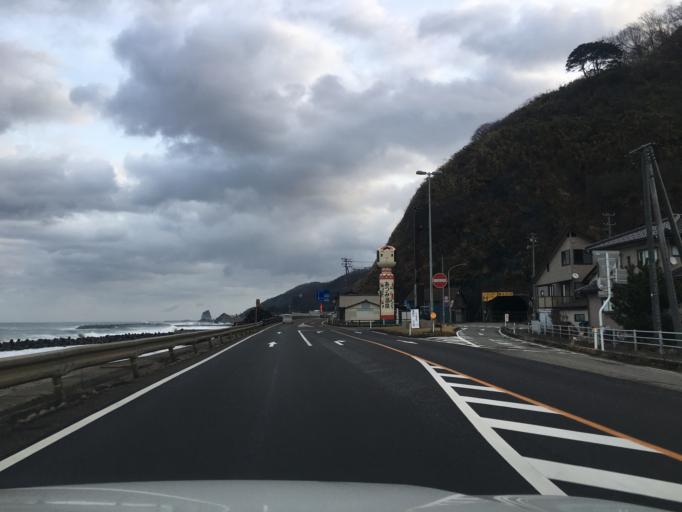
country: JP
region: Yamagata
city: Tsuruoka
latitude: 38.6194
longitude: 139.5831
